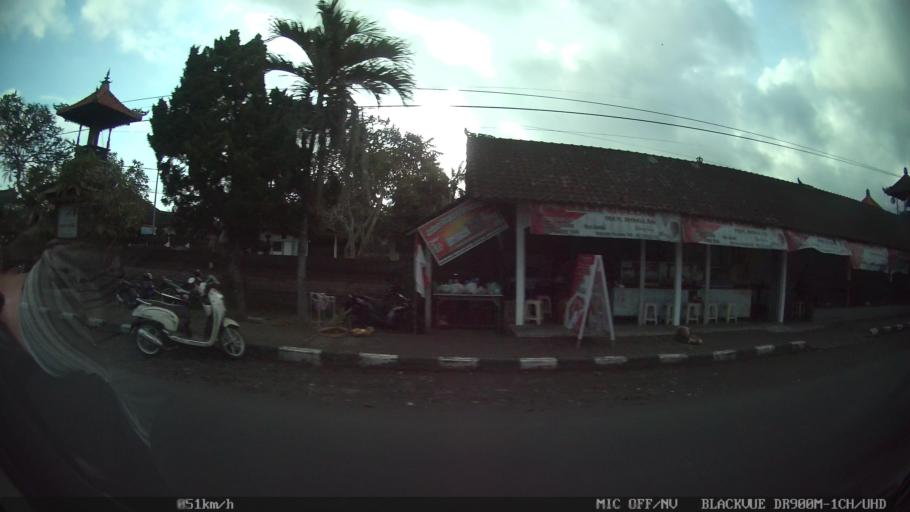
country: ID
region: Bali
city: Banjar Parekan
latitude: -8.5675
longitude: 115.2200
